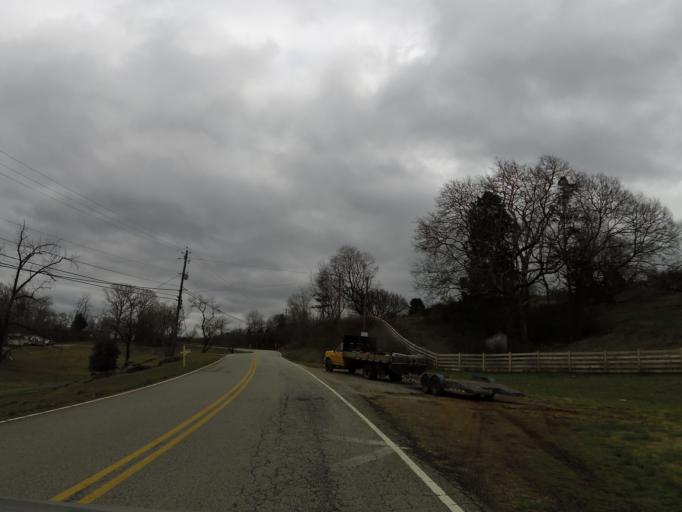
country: US
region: Tennessee
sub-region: Grainger County
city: Blaine
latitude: 36.1432
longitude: -83.6556
